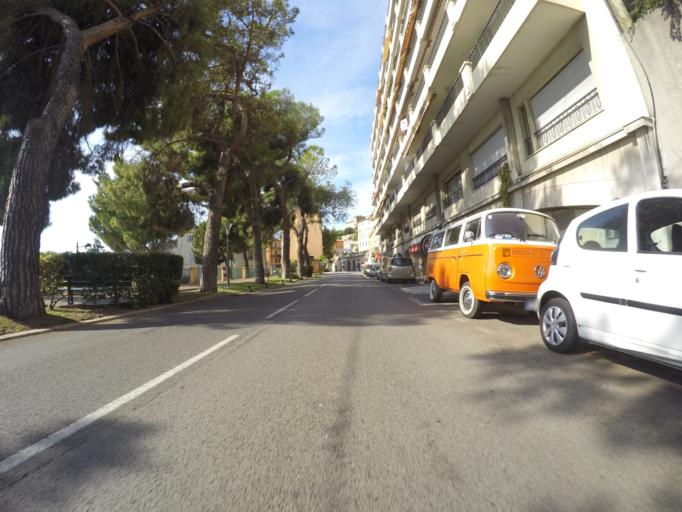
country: FR
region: Provence-Alpes-Cote d'Azur
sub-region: Departement des Alpes-Maritimes
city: Grasse
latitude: 43.6620
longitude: 6.9234
